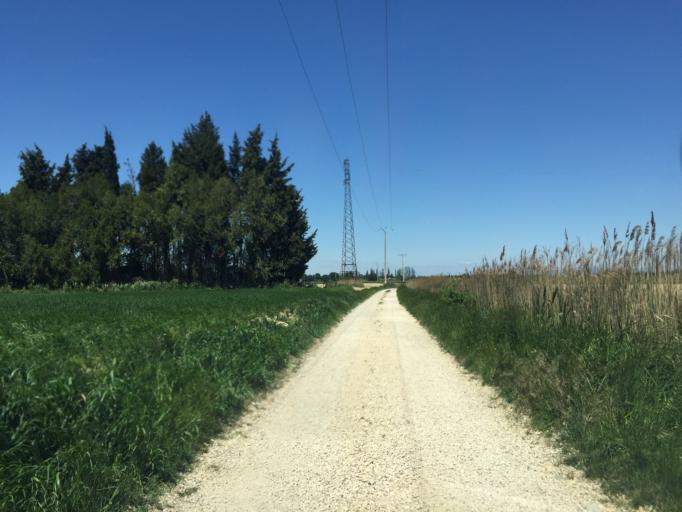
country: FR
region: Provence-Alpes-Cote d'Azur
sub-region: Departement du Vaucluse
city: Bedarrides
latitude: 44.0574
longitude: 4.9032
